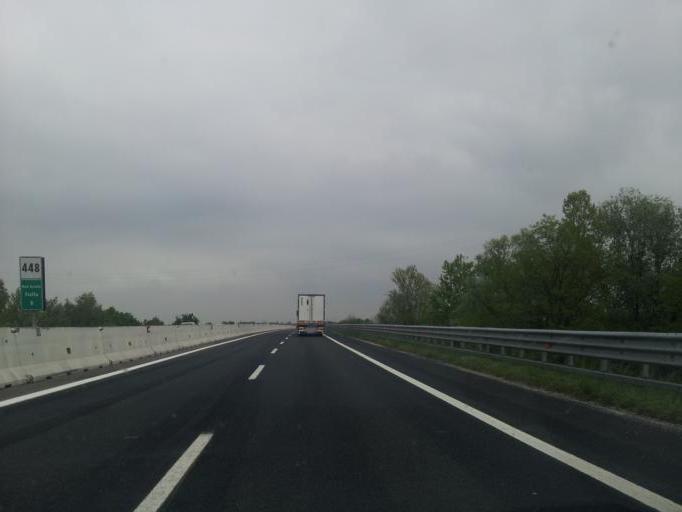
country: IT
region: Veneto
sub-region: Provincia di Venezia
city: Summaga
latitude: 45.7821
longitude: 12.7813
